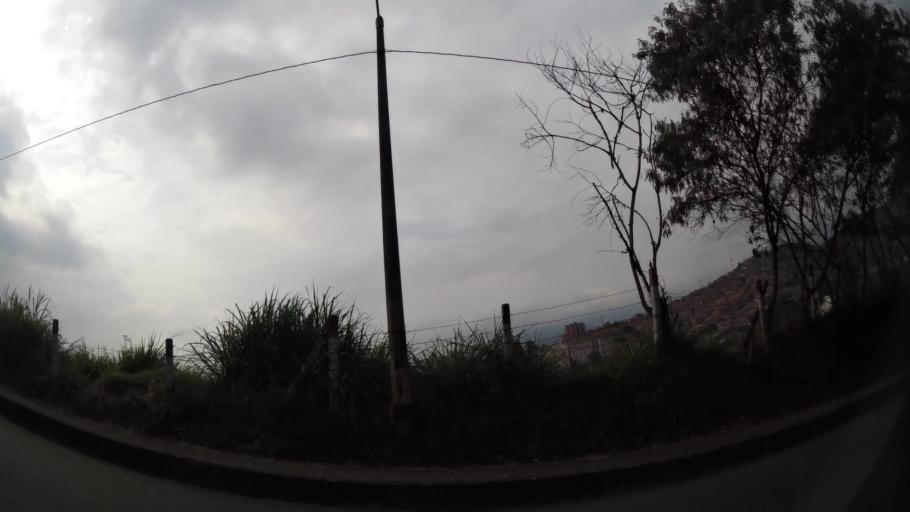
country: CO
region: Antioquia
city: Medellin
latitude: 6.2793
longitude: -75.6056
